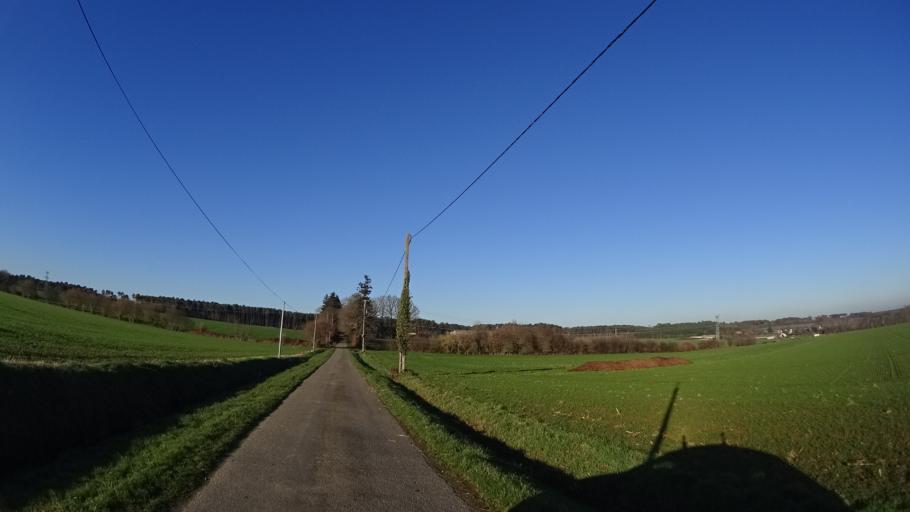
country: FR
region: Brittany
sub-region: Departement du Morbihan
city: Saint-Jacut-les-Pins
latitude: 47.6713
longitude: -2.1811
